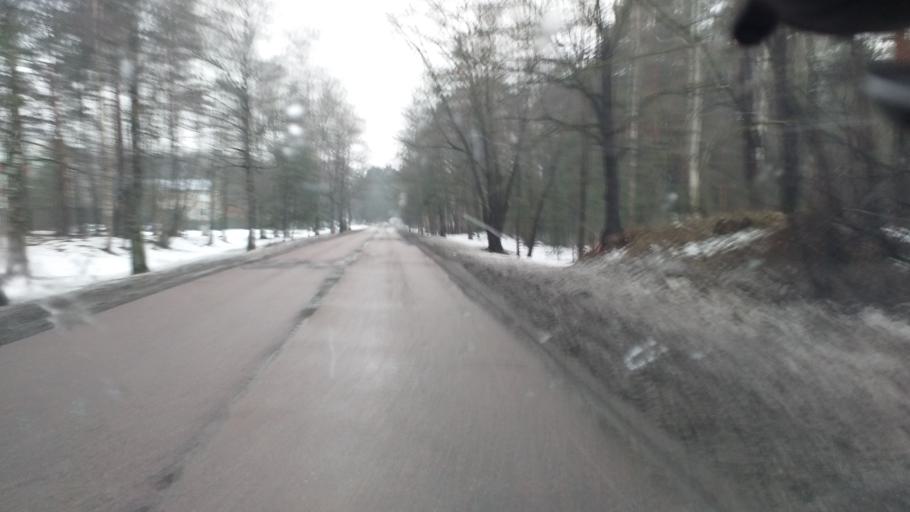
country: LV
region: Riga
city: Bolderaja
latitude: 56.9844
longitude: 24.0287
